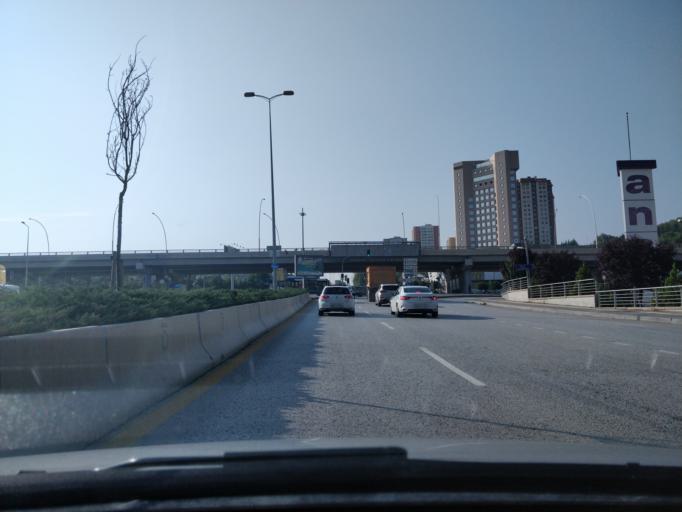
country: TR
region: Ankara
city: Etimesgut
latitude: 39.8957
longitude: 32.6783
